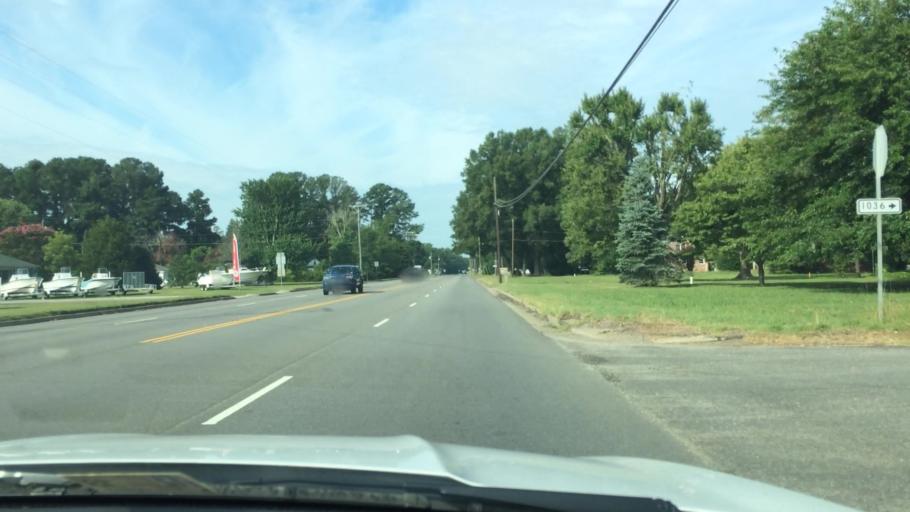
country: US
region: Virginia
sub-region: King William County
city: West Point
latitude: 37.5234
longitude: -76.8272
